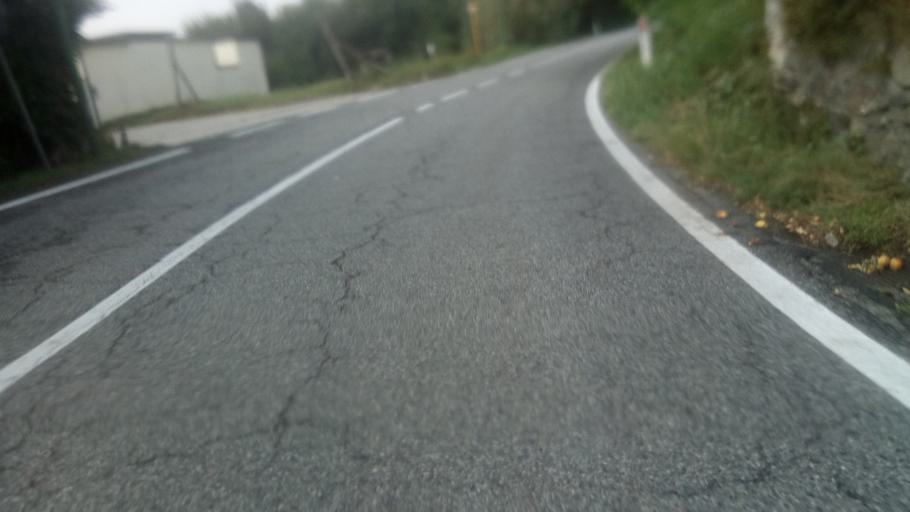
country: IT
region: Piedmont
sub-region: Provincia di Torino
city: Quagliuzzo
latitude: 45.4242
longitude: 7.7765
